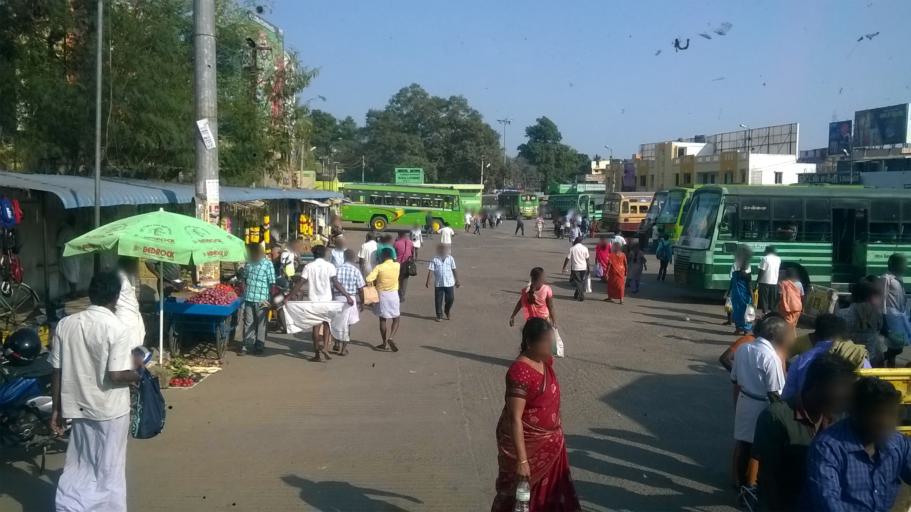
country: IN
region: Tamil Nadu
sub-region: Kancheepuram
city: Kanchipuram
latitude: 12.8358
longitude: 79.7055
